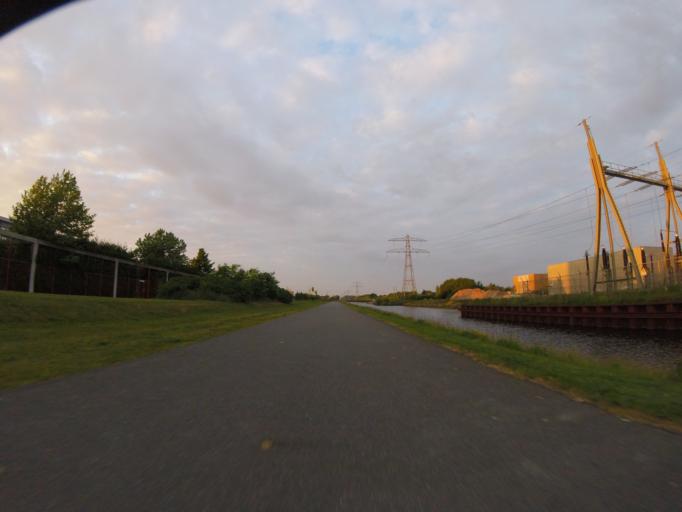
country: NL
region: North Holland
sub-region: Gemeente Heemstede
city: Heemstede
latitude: 52.3116
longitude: 4.6416
